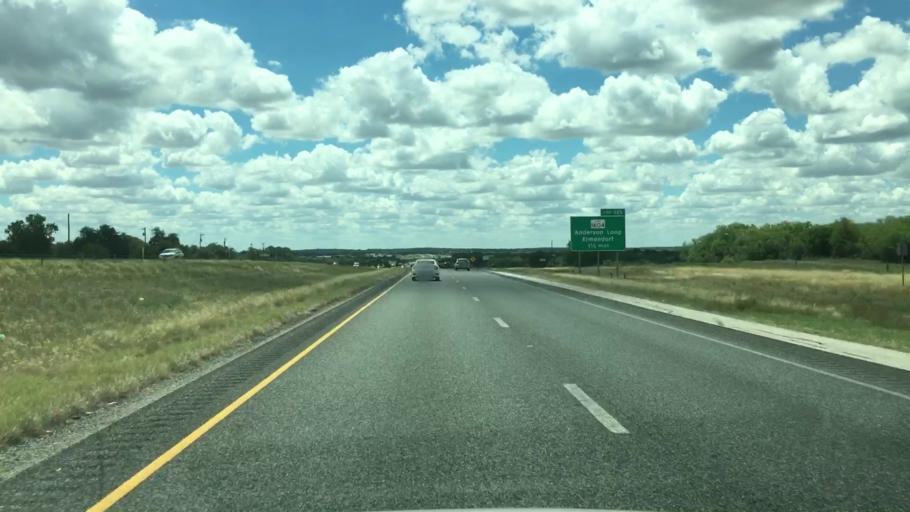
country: US
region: Texas
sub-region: Bexar County
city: Elmendorf
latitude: 29.2430
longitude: -98.3986
